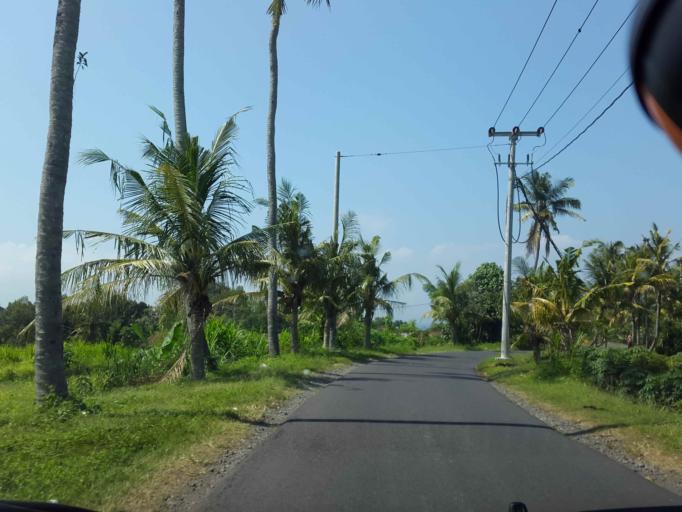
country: ID
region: Bali
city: Klungkung
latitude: -8.5640
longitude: 115.3730
